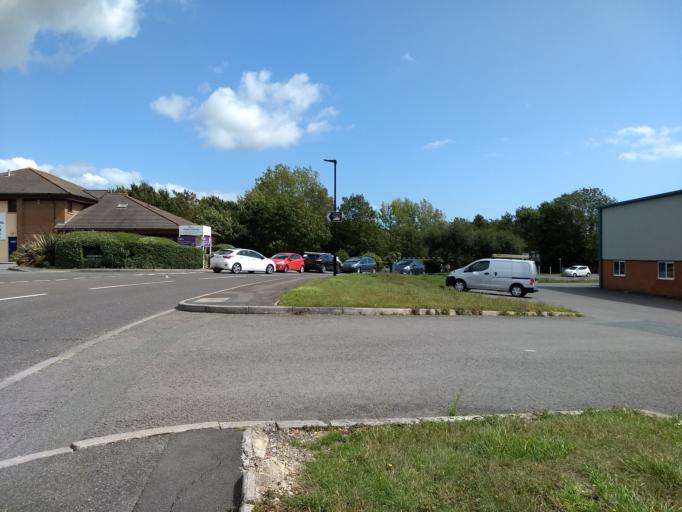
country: GB
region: England
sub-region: Isle of Wight
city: Newport
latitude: 50.7092
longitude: -1.2933
